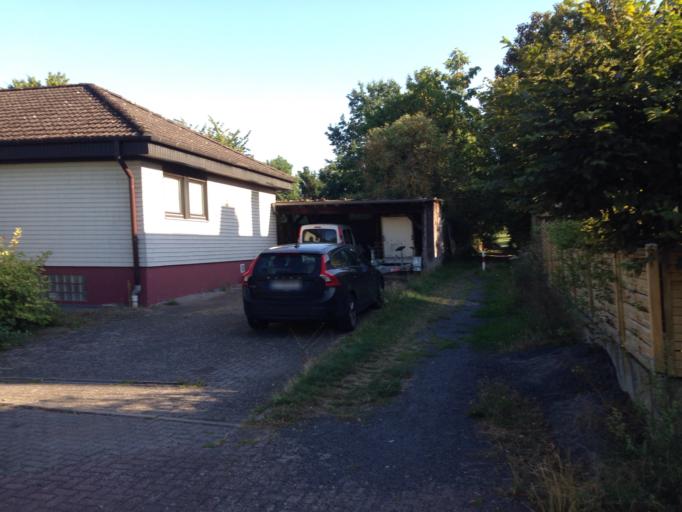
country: DE
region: Hesse
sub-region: Regierungsbezirk Giessen
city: Lich
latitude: 50.5325
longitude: 8.7511
